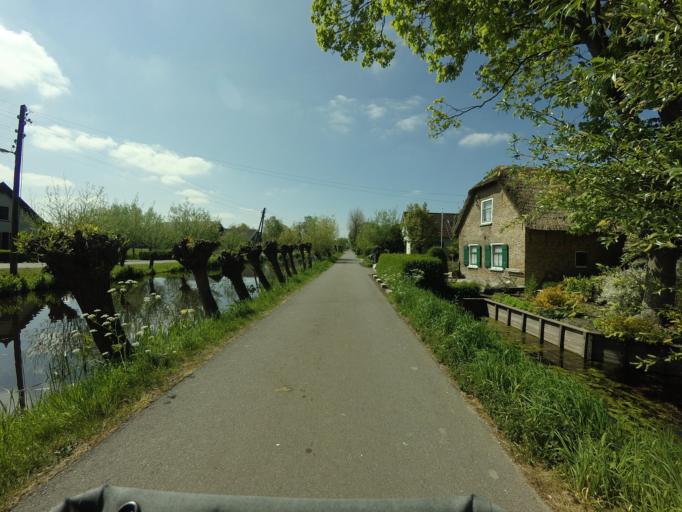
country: NL
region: South Holland
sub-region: Gemeente Gouda
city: Gouda
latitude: 51.9813
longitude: 4.7263
